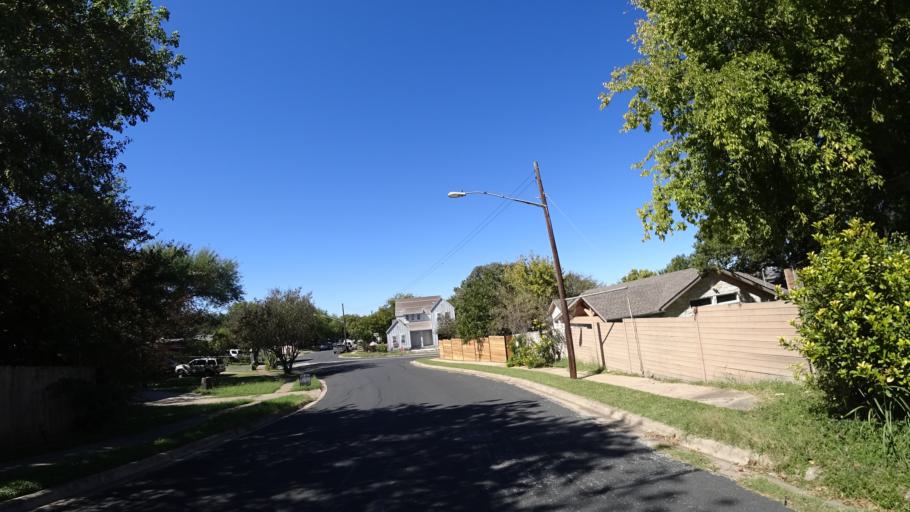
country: US
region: Texas
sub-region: Travis County
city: Austin
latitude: 30.2318
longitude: -97.7698
